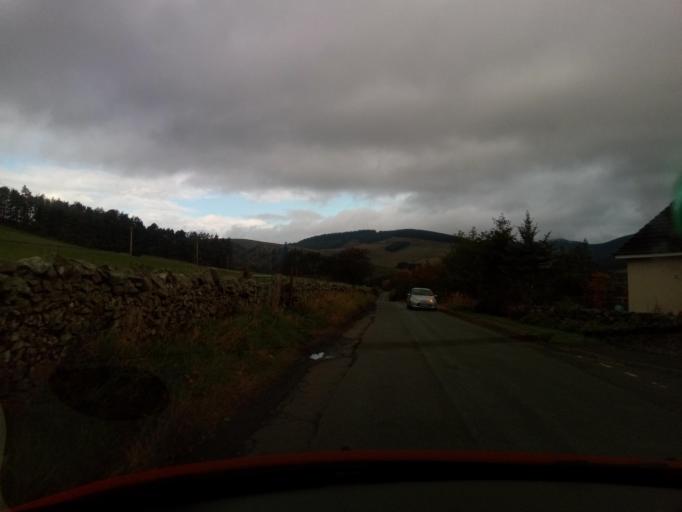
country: GB
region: Scotland
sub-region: The Scottish Borders
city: Innerleithen
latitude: 55.6352
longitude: -3.1068
